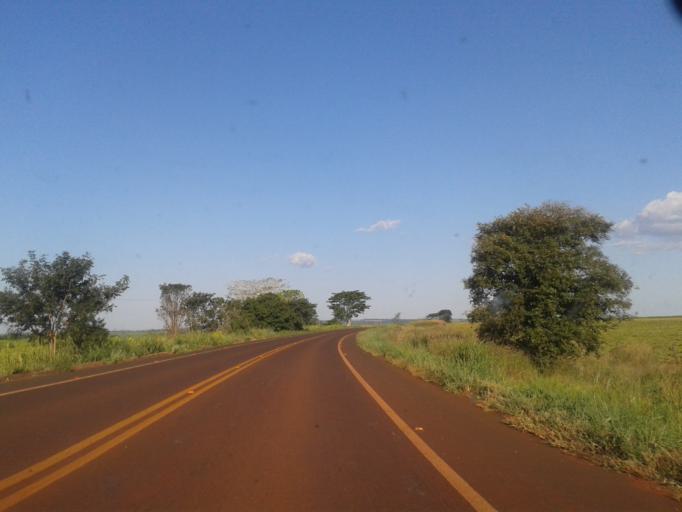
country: BR
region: Minas Gerais
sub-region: Santa Vitoria
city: Santa Vitoria
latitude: -18.6922
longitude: -49.8847
